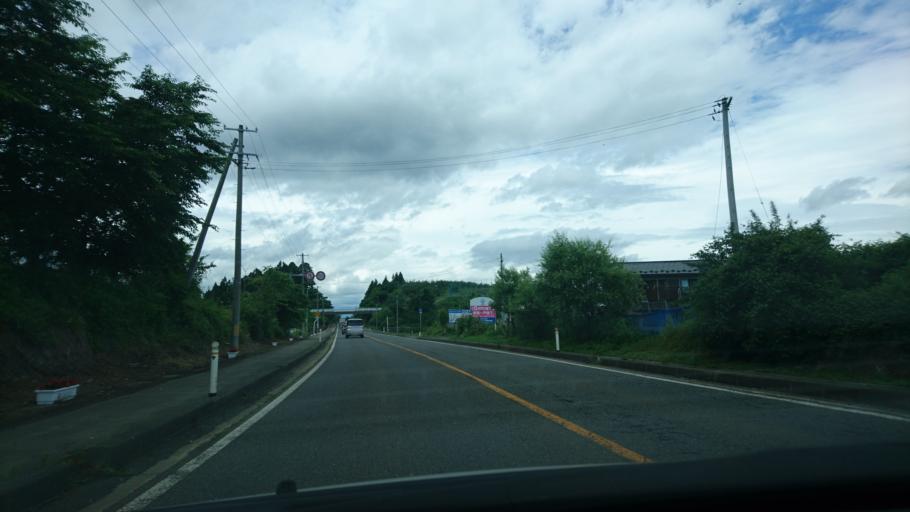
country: JP
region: Iwate
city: Morioka-shi
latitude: 39.6110
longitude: 141.2022
